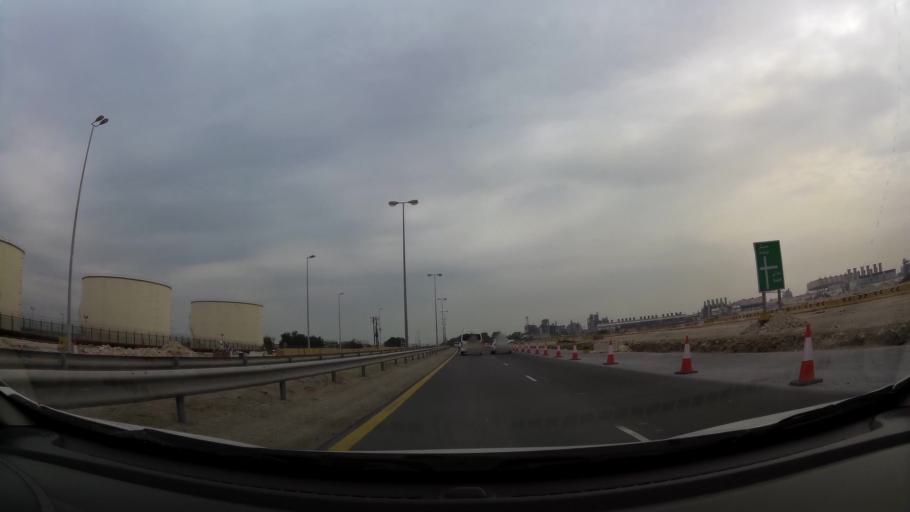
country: BH
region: Northern
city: Sitrah
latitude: 26.1010
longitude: 50.6037
